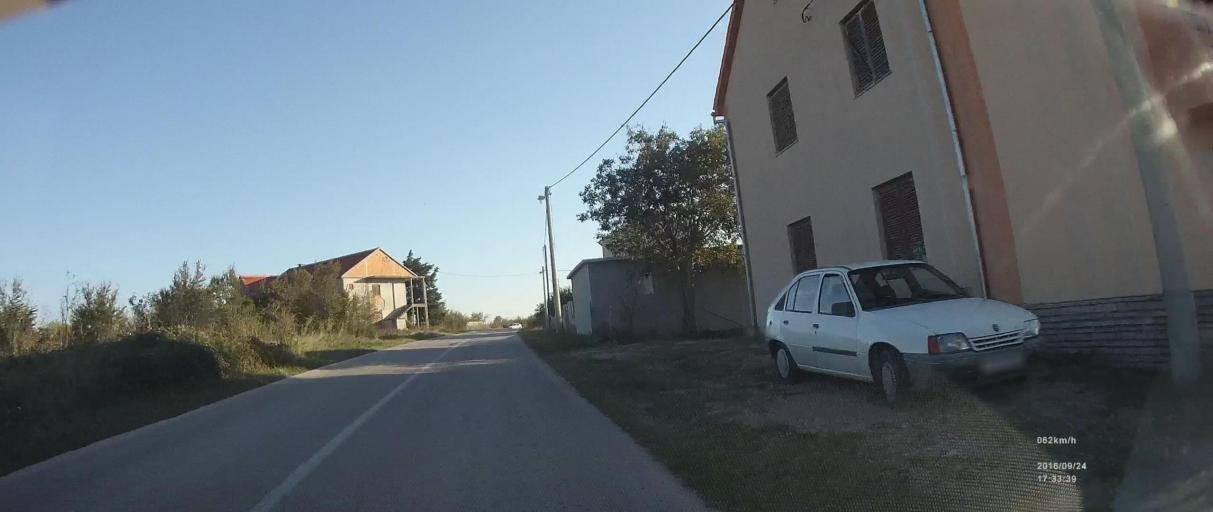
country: HR
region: Zadarska
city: Posedarje
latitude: 44.1723
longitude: 15.4576
